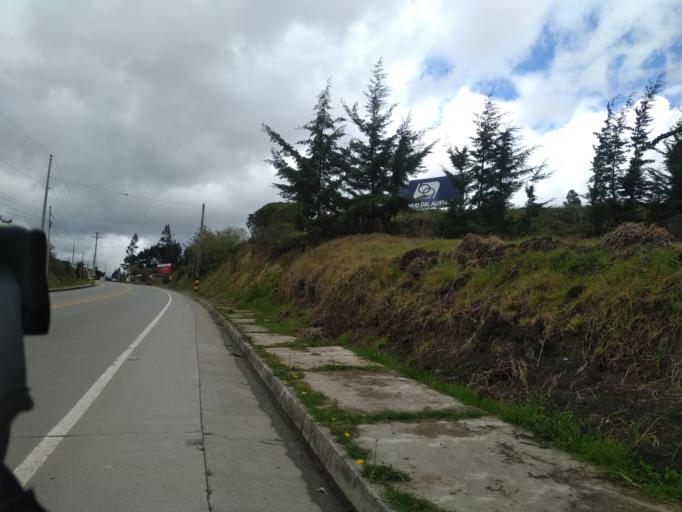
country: EC
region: Loja
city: Loja
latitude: -3.9531
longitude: -79.2504
